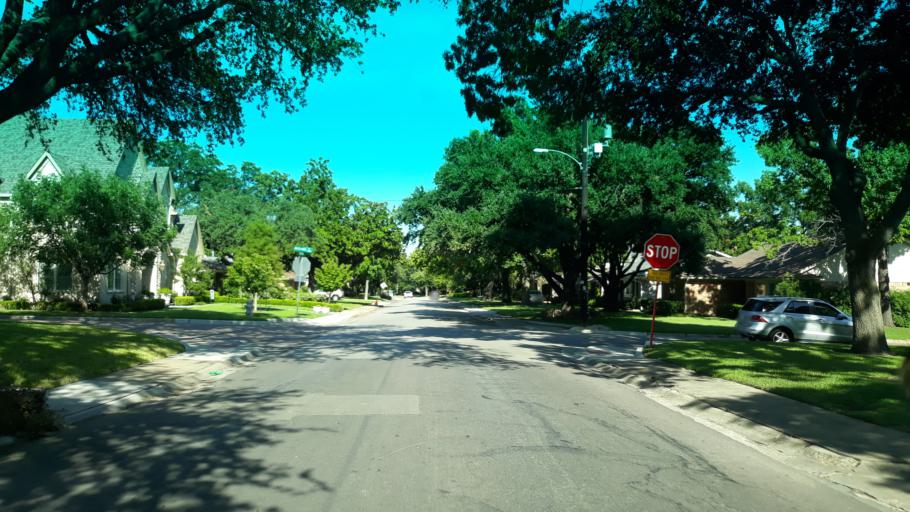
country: US
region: Texas
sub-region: Dallas County
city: Highland Park
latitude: 32.8266
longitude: -96.7503
